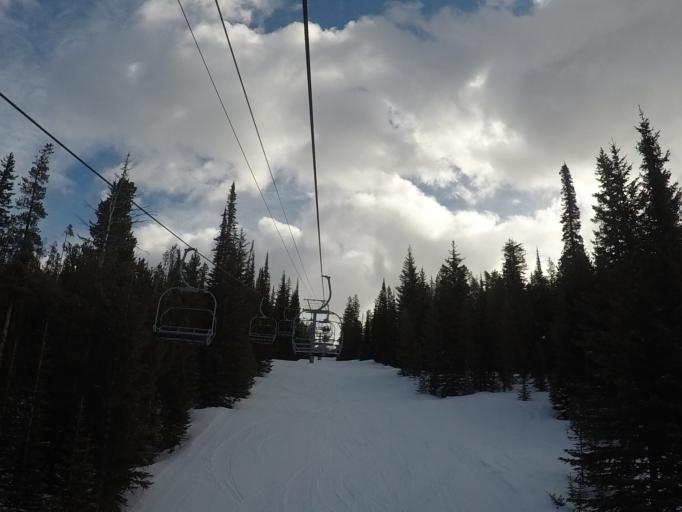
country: US
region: Montana
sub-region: Granite County
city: Philipsburg
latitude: 46.2521
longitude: -113.2257
